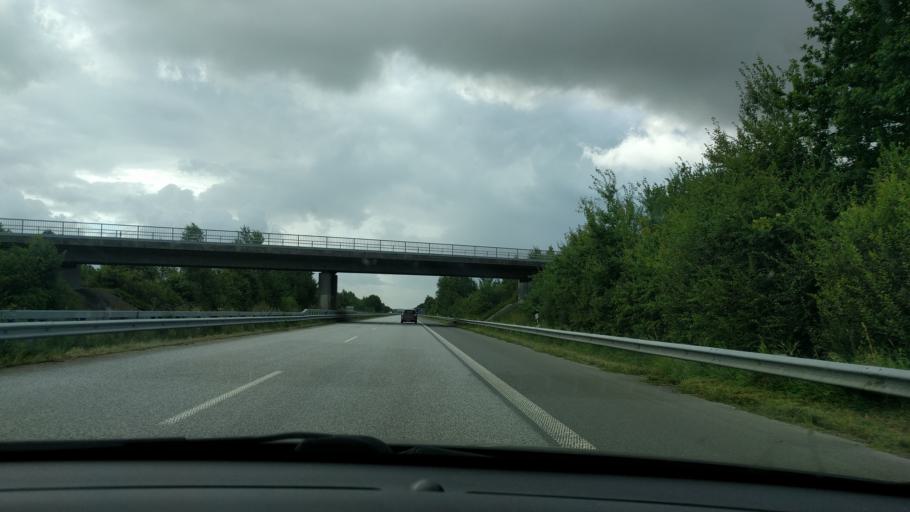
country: DE
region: Schleswig-Holstein
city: Tensbuttel-Rost
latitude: 54.1289
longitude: 9.2544
